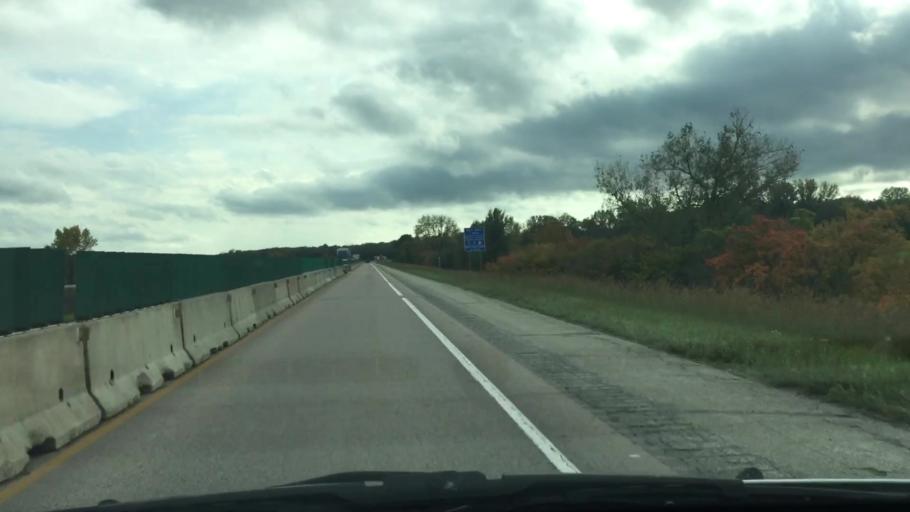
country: US
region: Iowa
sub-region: Decatur County
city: Lamoni
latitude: 40.6726
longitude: -93.8504
